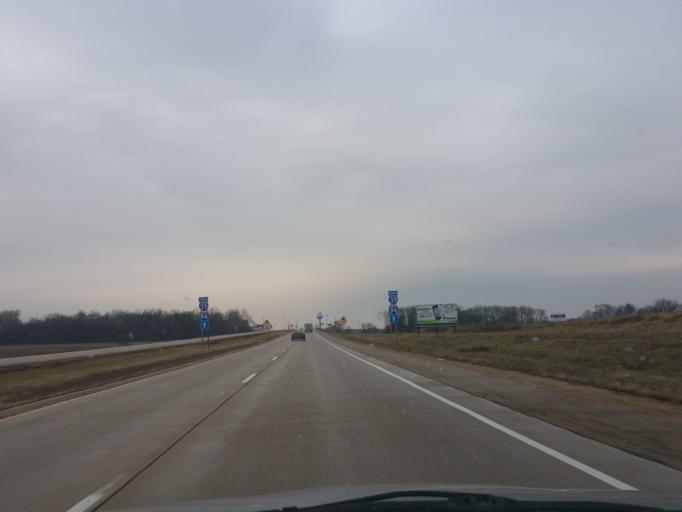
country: US
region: Wisconsin
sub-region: Dane County
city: Windsor
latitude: 43.1584
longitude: -89.3245
